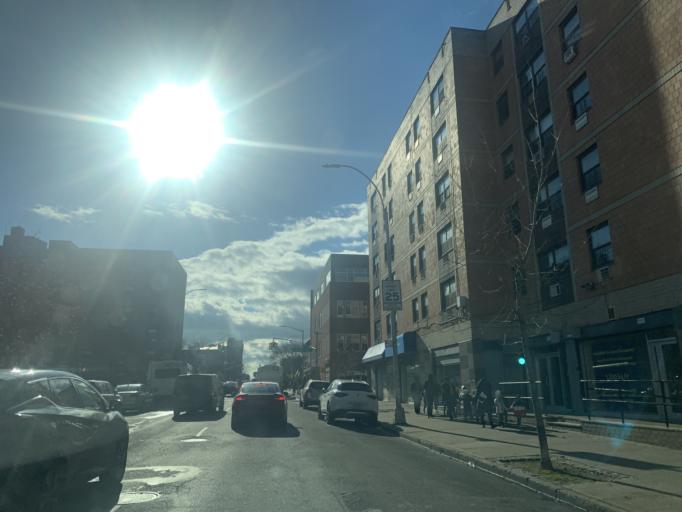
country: US
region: New York
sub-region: Kings County
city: Brooklyn
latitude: 40.6882
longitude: -73.9391
